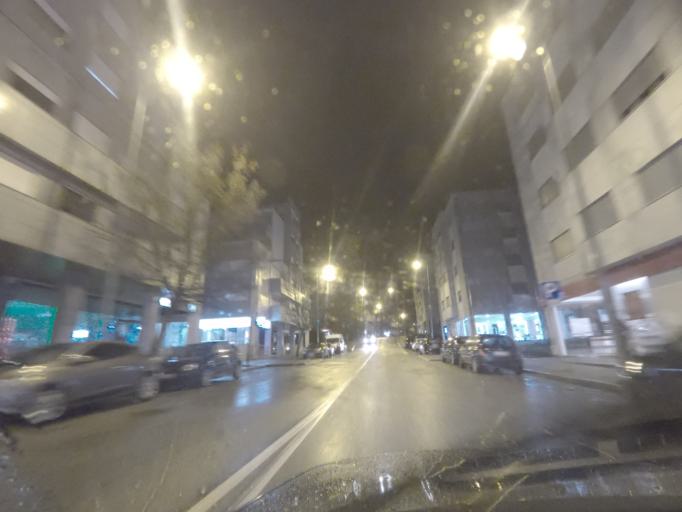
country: PT
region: Vila Real
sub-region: Vila Real
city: Vila Real
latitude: 41.2955
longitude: -7.7334
